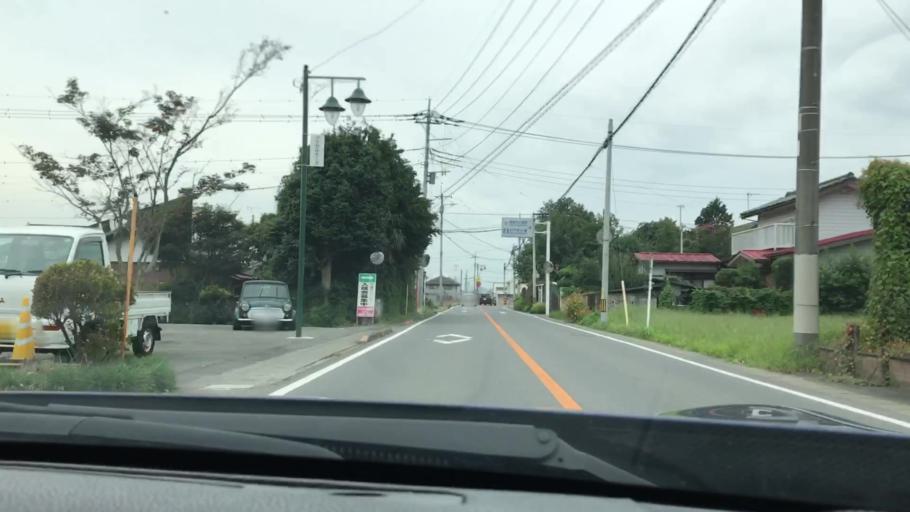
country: JP
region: Gunma
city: Kanekomachi
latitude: 36.3956
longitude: 138.9962
